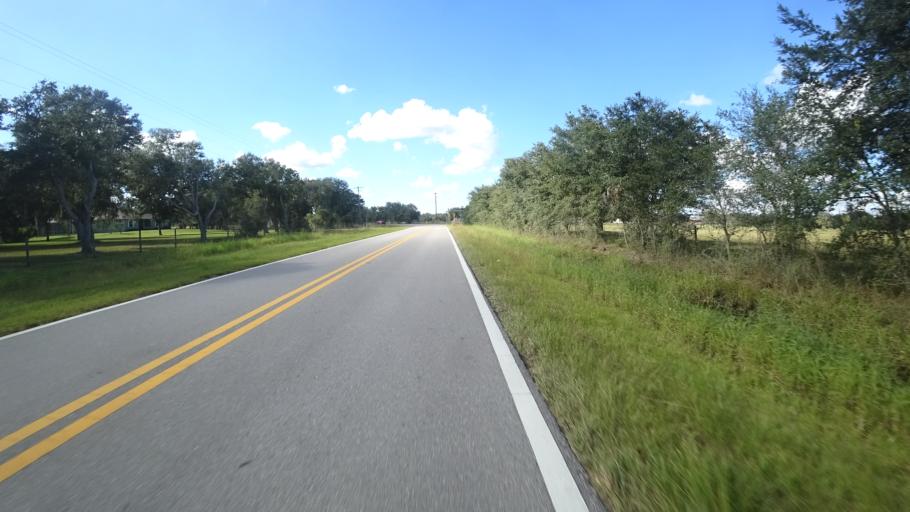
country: US
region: Florida
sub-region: Sarasota County
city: Lake Sarasota
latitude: 27.2896
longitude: -82.2339
